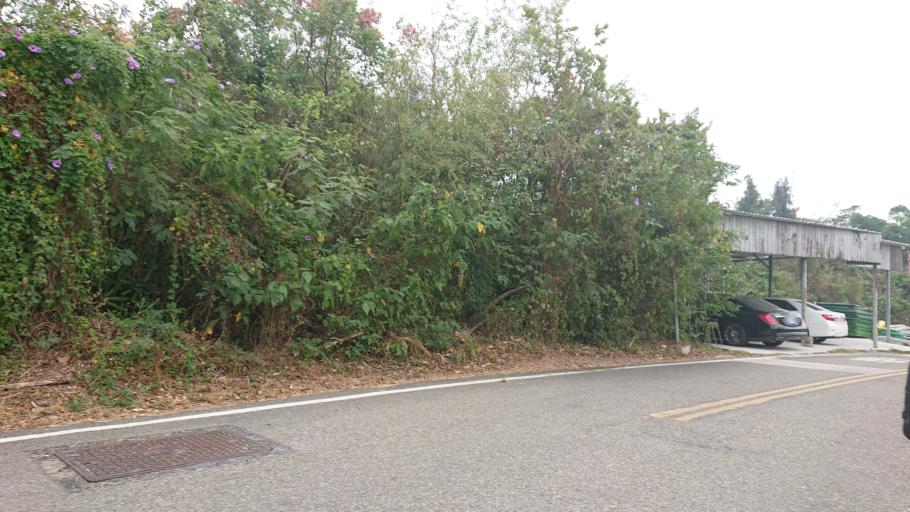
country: TW
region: Fukien
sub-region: Kinmen
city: Jincheng
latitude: 24.4494
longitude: 118.3862
